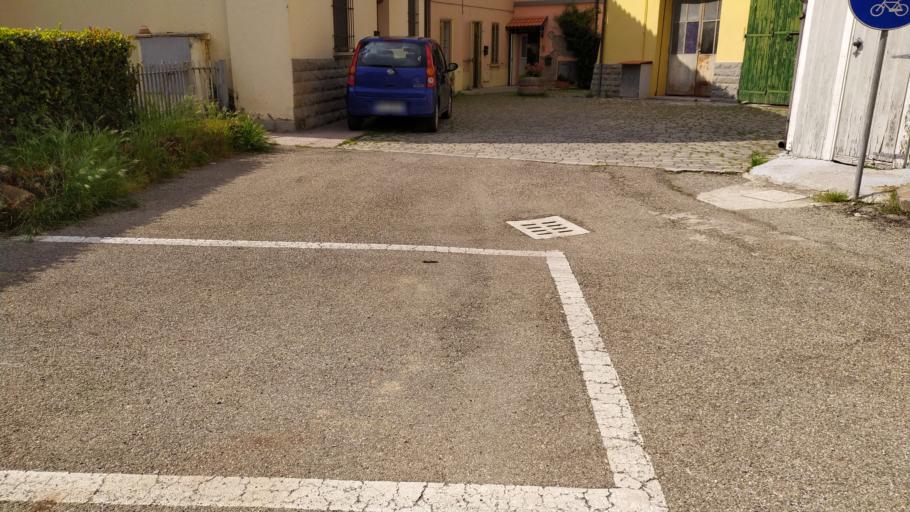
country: IT
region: Emilia-Romagna
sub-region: Provincia di Bologna
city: Borgo Tossignano
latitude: 44.2771
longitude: 11.5864
